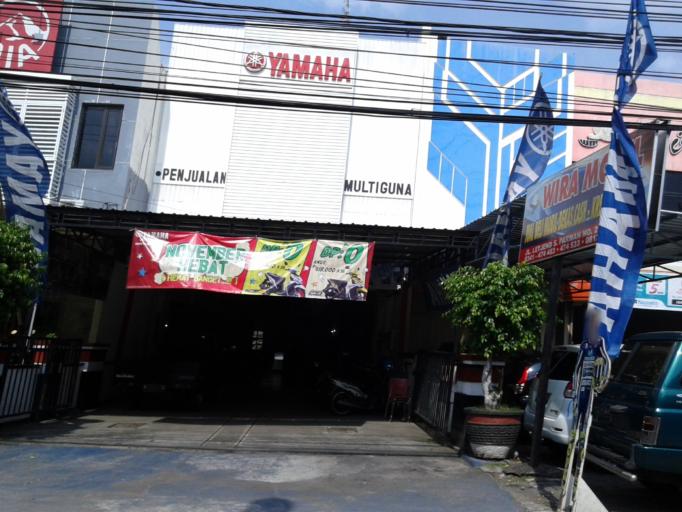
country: ID
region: East Java
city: Malang
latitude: -7.9557
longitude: 112.6360
